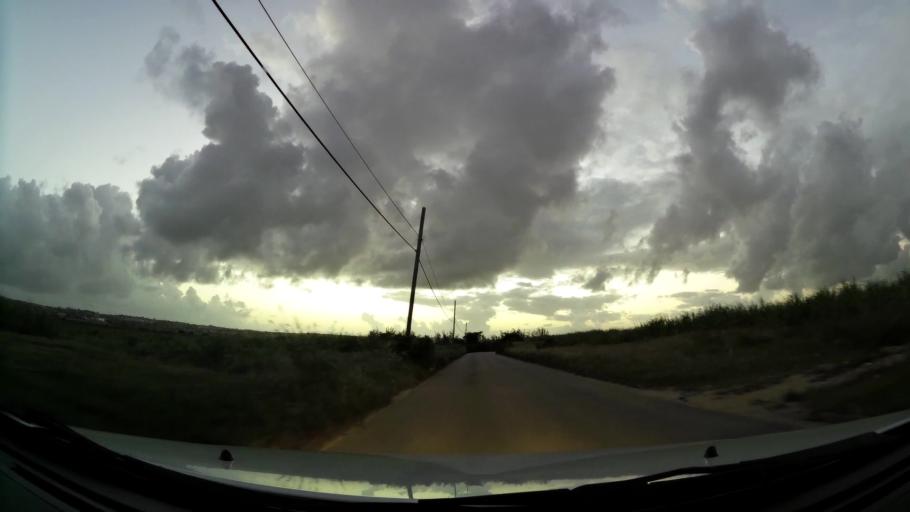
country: BB
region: Saint Philip
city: Crane
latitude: 13.1184
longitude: -59.4870
